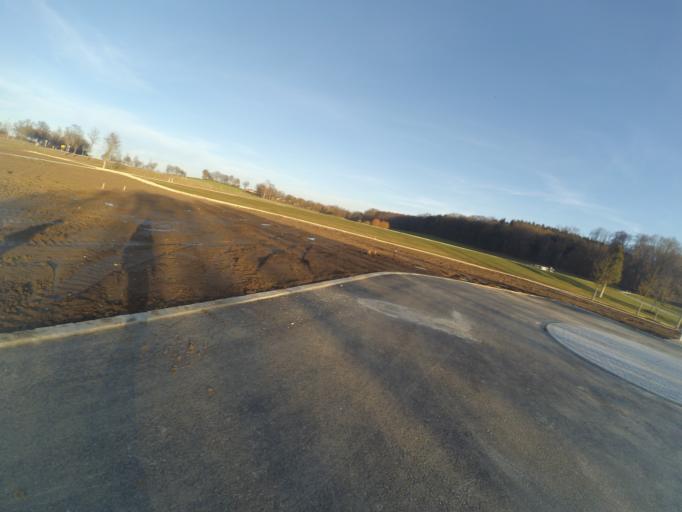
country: DE
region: Bavaria
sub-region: Swabia
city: Guenzburg
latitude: 48.4508
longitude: 10.3004
